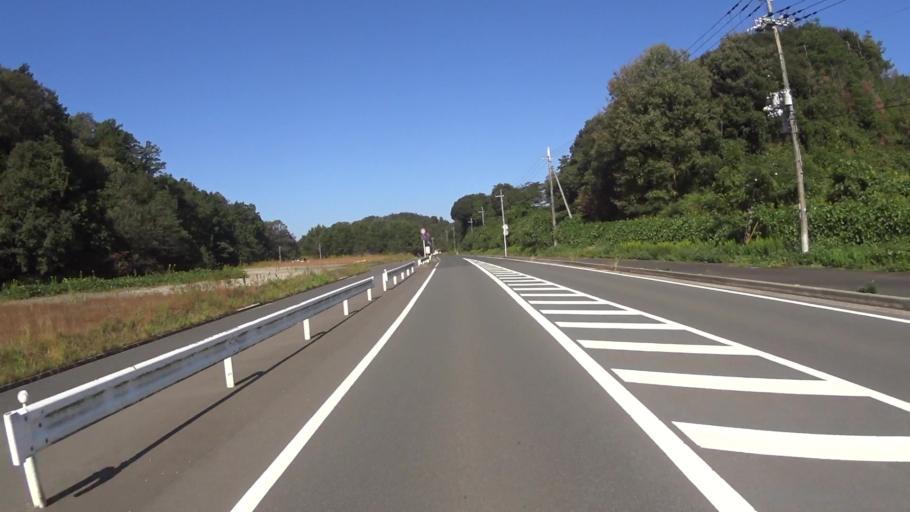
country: JP
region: Kyoto
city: Miyazu
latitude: 35.6780
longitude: 135.0706
